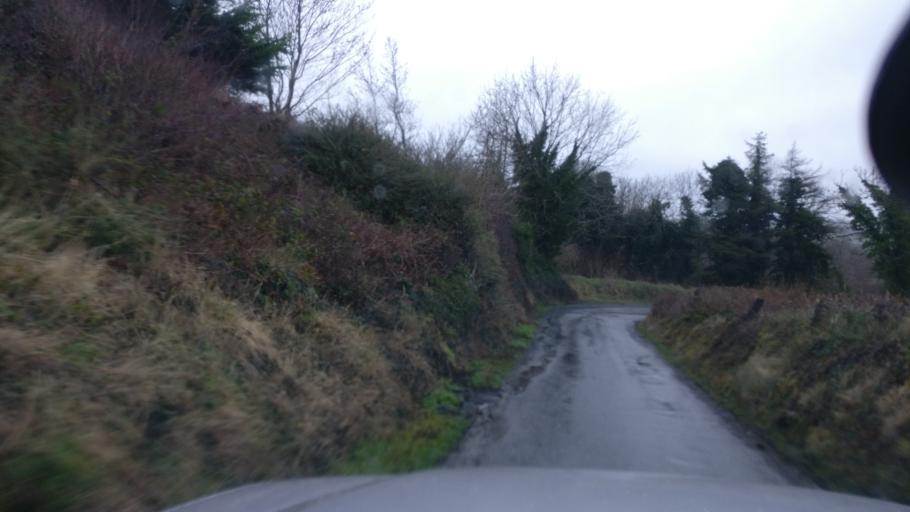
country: IE
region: Connaught
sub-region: County Galway
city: Loughrea
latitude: 53.1525
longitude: -8.6357
